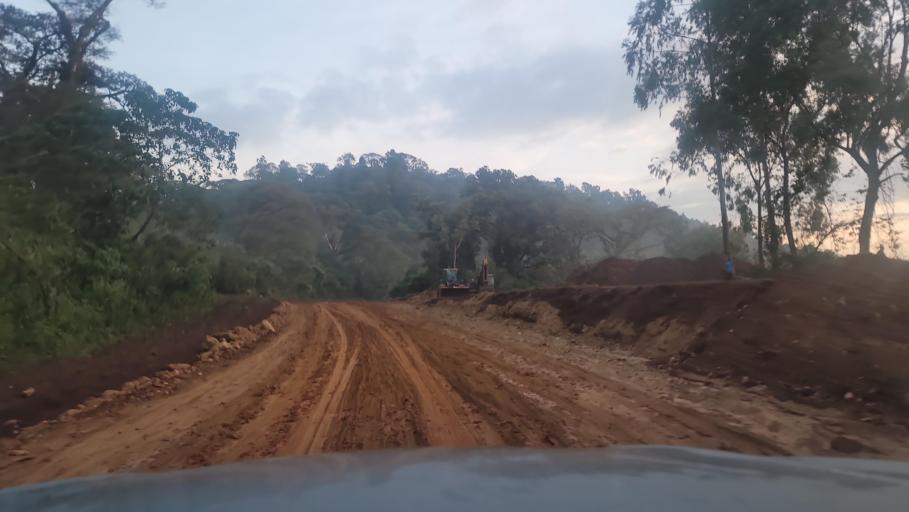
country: ET
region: Oromiya
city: Agaro
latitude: 7.7933
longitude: 36.3685
